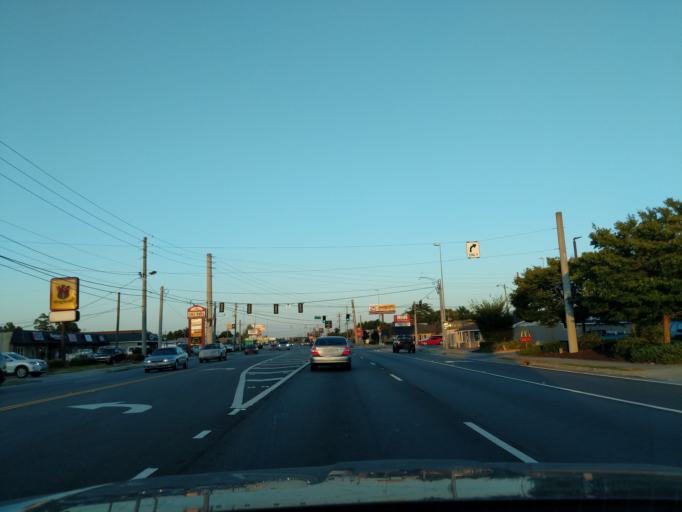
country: US
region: Georgia
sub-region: Columbia County
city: Martinez
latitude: 33.5128
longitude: -82.0872
